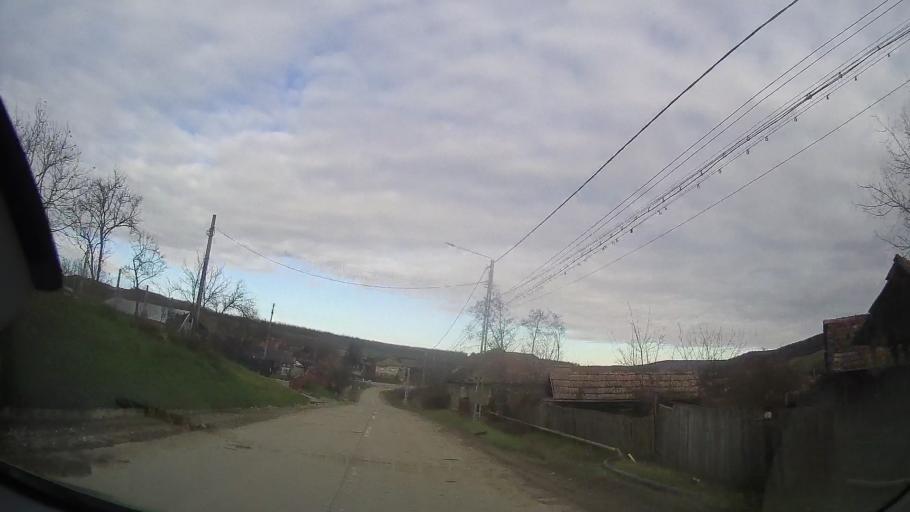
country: RO
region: Bistrita-Nasaud
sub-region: Comuna Sanmihaiu de Campie
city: Sanmihaiu de Campie
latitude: 46.8958
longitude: 24.3367
